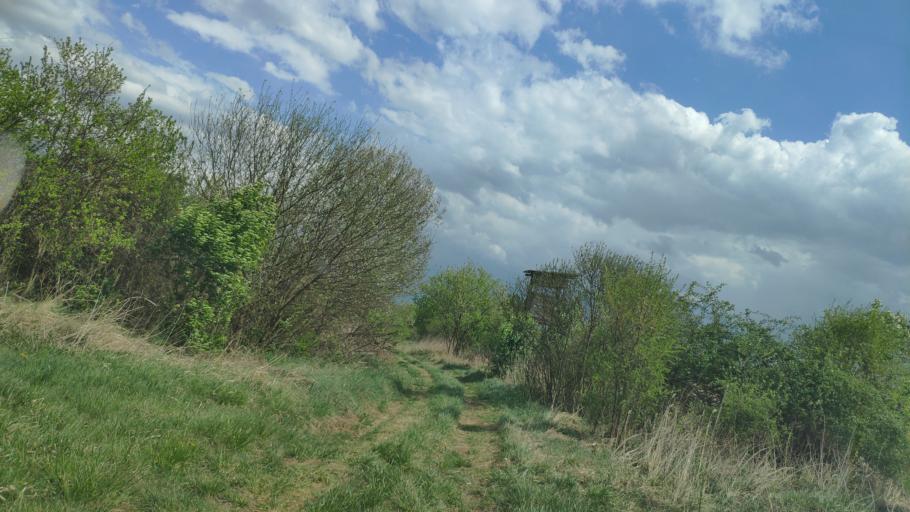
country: SK
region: Kosicky
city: Moldava nad Bodvou
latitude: 48.5557
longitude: 20.9512
